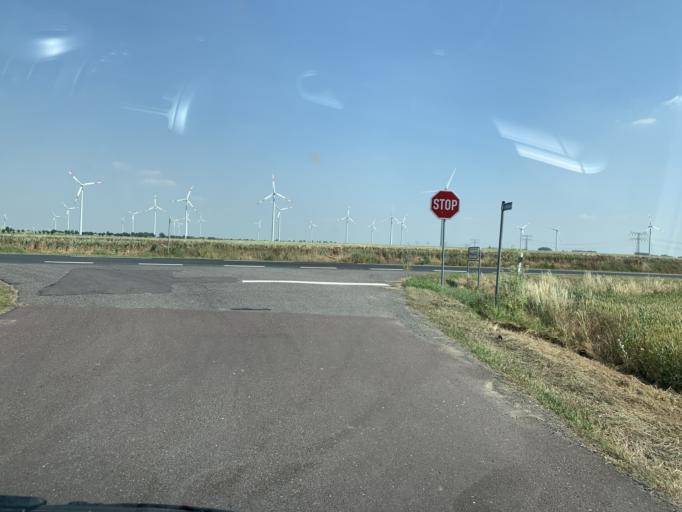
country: DE
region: Saxony-Anhalt
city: Erxleben
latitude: 52.1735
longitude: 11.2681
